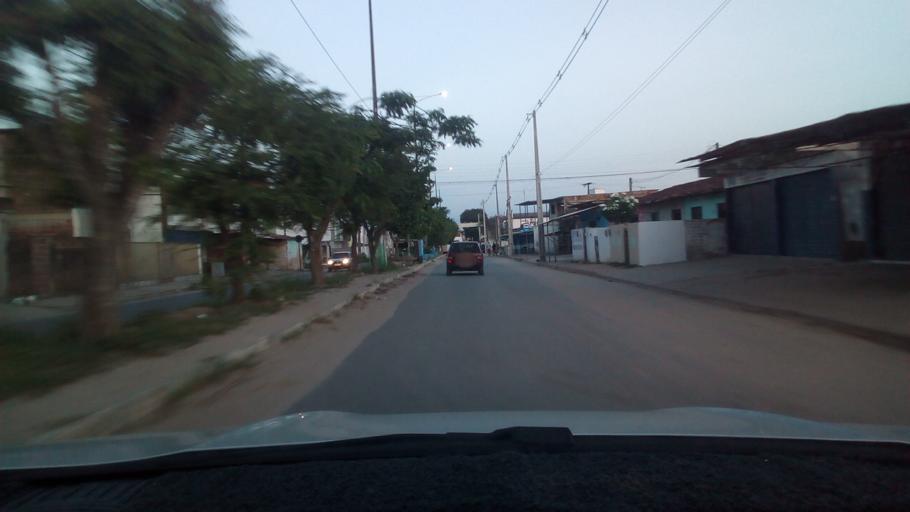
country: BR
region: Paraiba
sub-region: Bayeux
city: Bayeux
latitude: -7.1776
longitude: -34.9237
